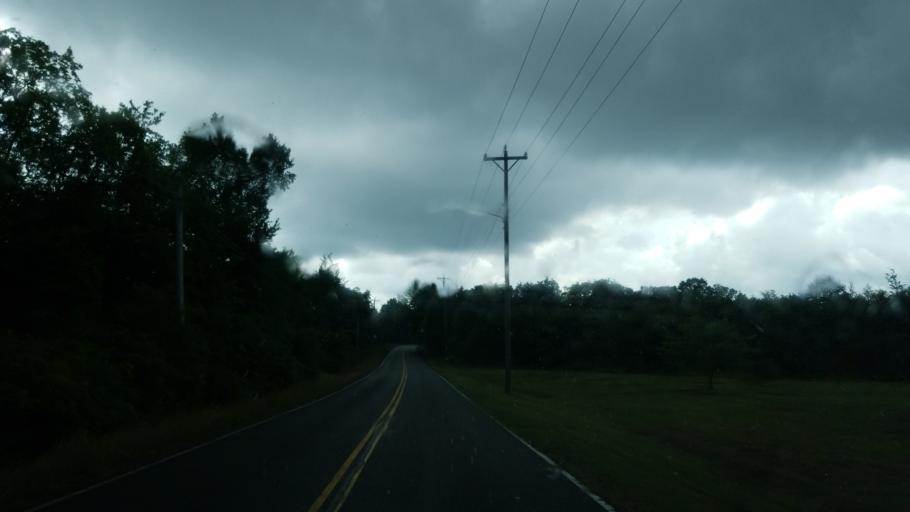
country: US
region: Tennessee
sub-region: Rutherford County
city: La Vergne
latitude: 36.0553
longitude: -86.5830
